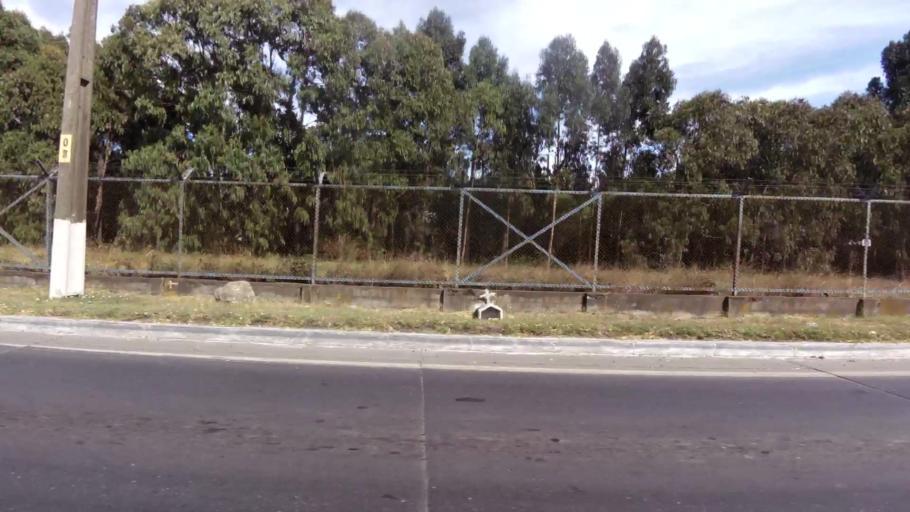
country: CL
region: Biobio
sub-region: Provincia de Concepcion
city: Talcahuano
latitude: -36.7362
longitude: -73.1203
